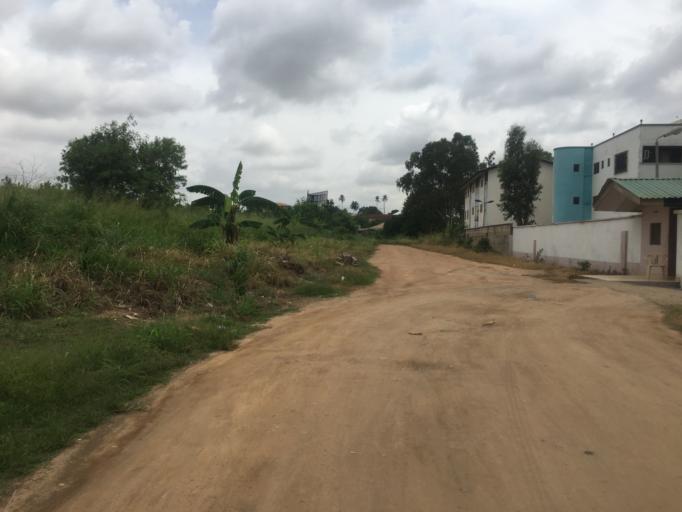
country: GH
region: Ashanti
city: Mamponteng
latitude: 6.6893
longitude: -1.5532
